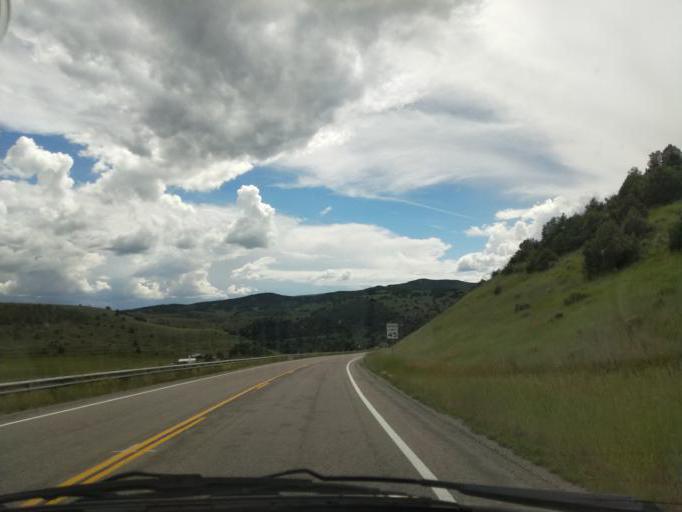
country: US
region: Colorado
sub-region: Delta County
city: Paonia
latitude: 39.0839
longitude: -107.3639
